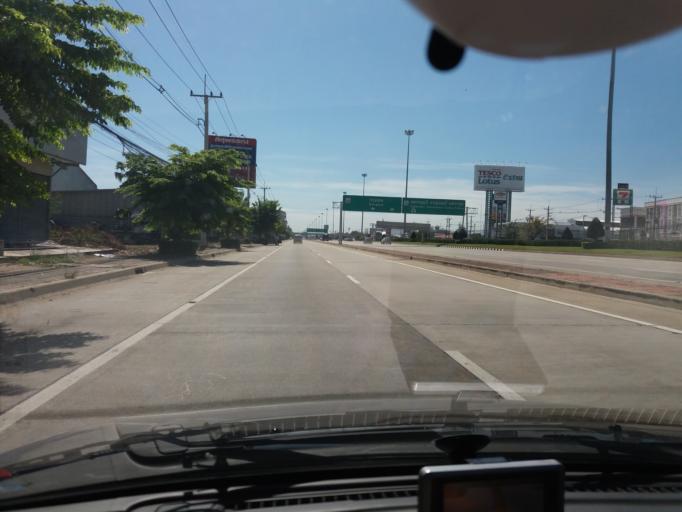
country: TH
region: Suphan Buri
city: Suphan Buri
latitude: 14.4724
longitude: 100.1318
